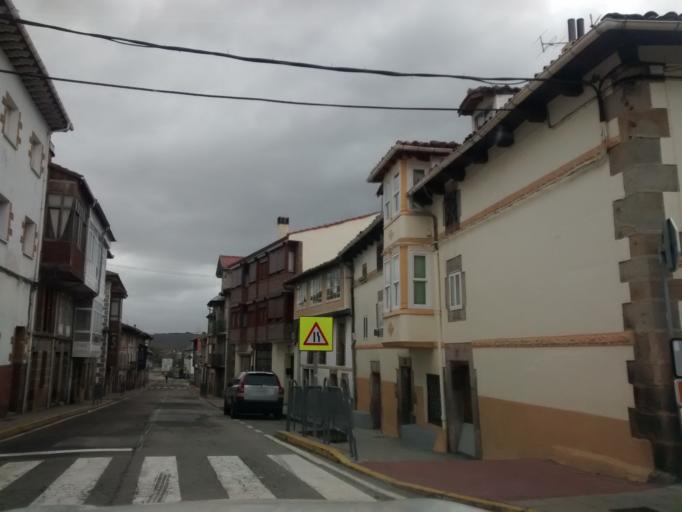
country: ES
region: Cantabria
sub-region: Provincia de Cantabria
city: San Pedro del Romeral
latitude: 42.9701
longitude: -3.7863
